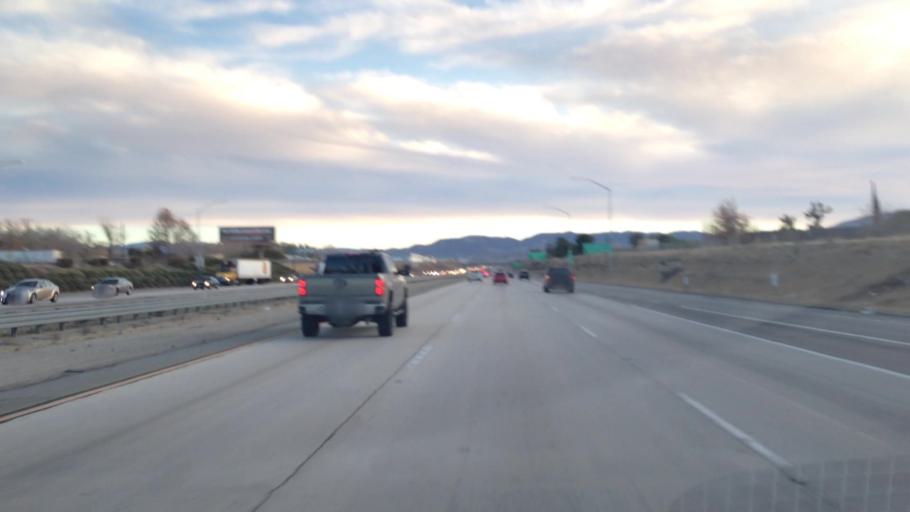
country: US
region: California
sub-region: Los Angeles County
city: Lancaster
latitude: 34.6581
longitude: -118.1535
